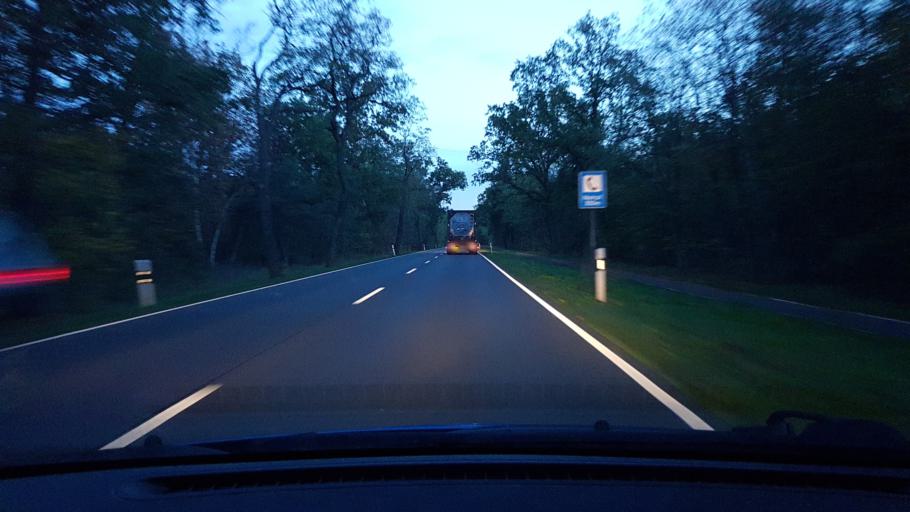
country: DE
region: Saxony-Anhalt
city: Zerbst
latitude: 51.9470
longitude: 12.1122
